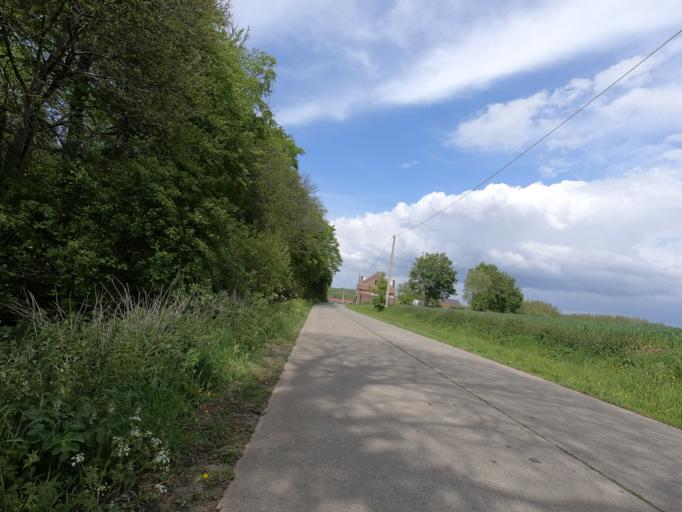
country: BE
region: Flanders
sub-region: Provincie Oost-Vlaanderen
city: Ronse
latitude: 50.7693
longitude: 3.5771
